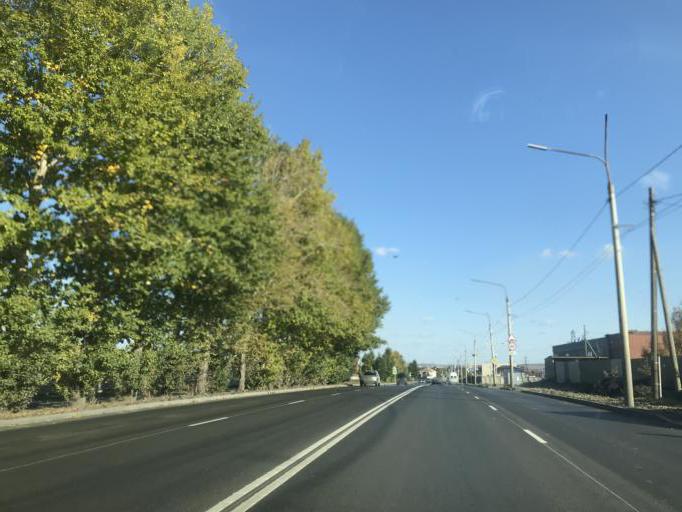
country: RU
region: Chelyabinsk
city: Roshchino
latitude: 55.2346
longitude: 61.3095
